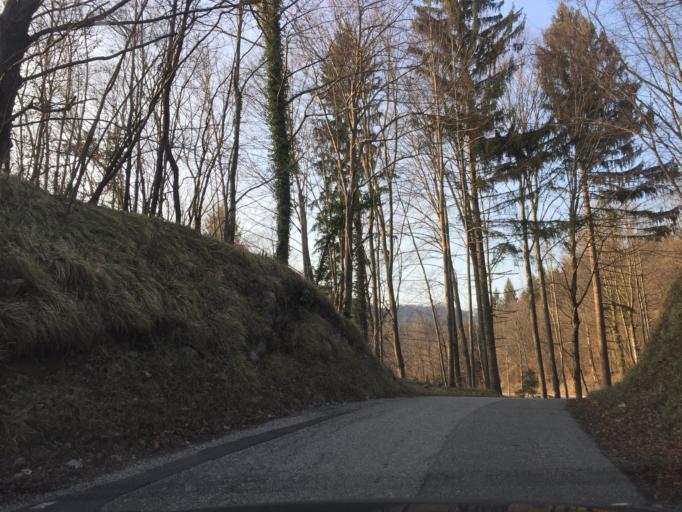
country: SI
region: Kanal
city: Kanal
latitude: 46.0518
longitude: 13.6693
